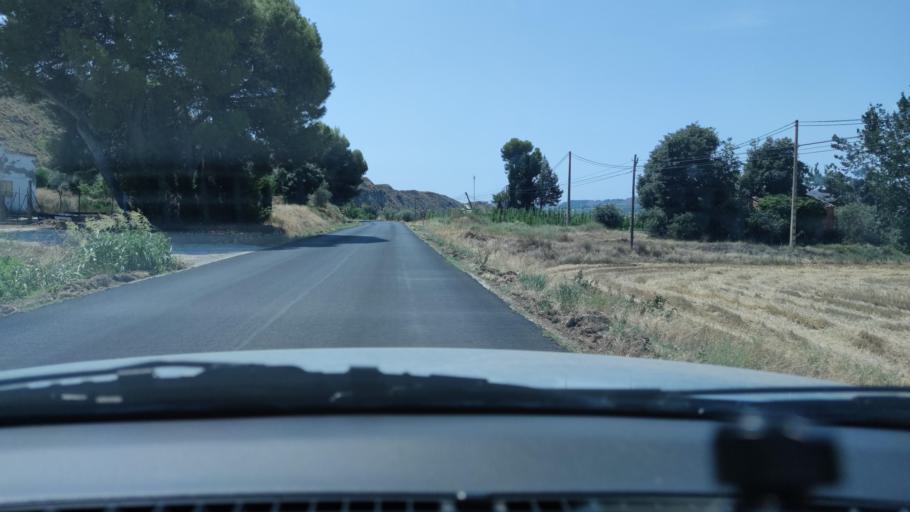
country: ES
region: Catalonia
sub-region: Provincia de Lleida
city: Alfarras
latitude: 41.8387
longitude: 0.5833
